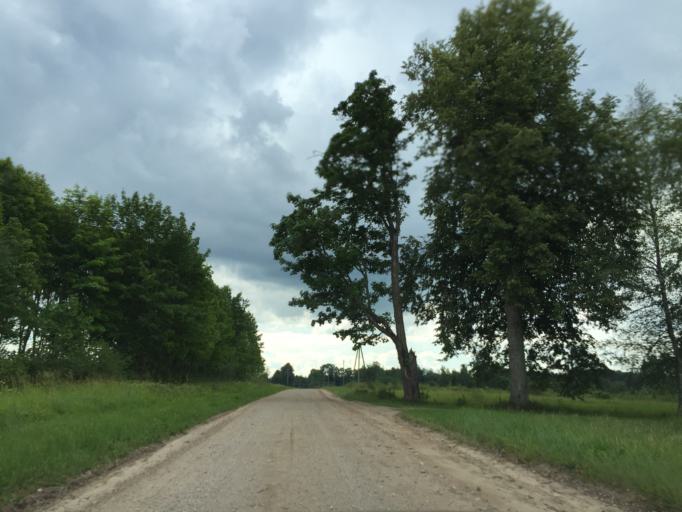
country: LV
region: Ligatne
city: Ligatne
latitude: 57.2229
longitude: 25.0349
